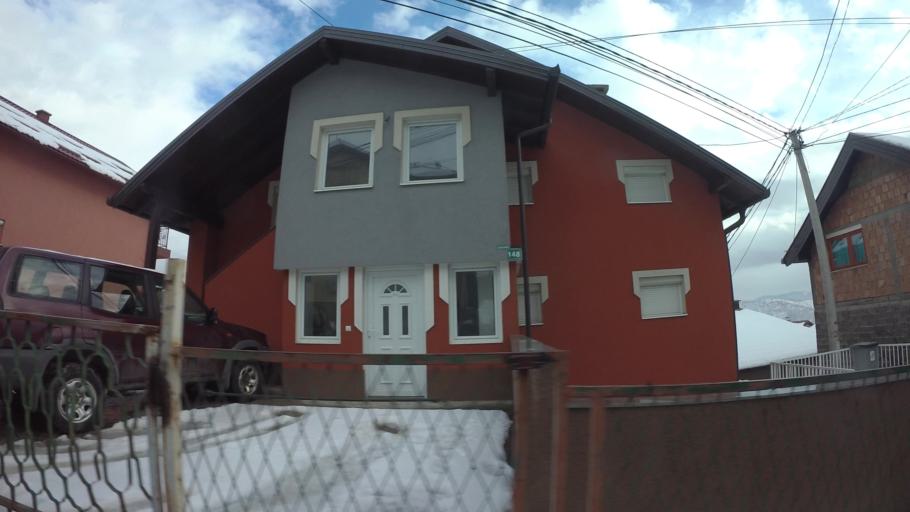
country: BA
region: Federation of Bosnia and Herzegovina
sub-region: Kanton Sarajevo
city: Sarajevo
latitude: 43.8604
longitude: 18.3448
